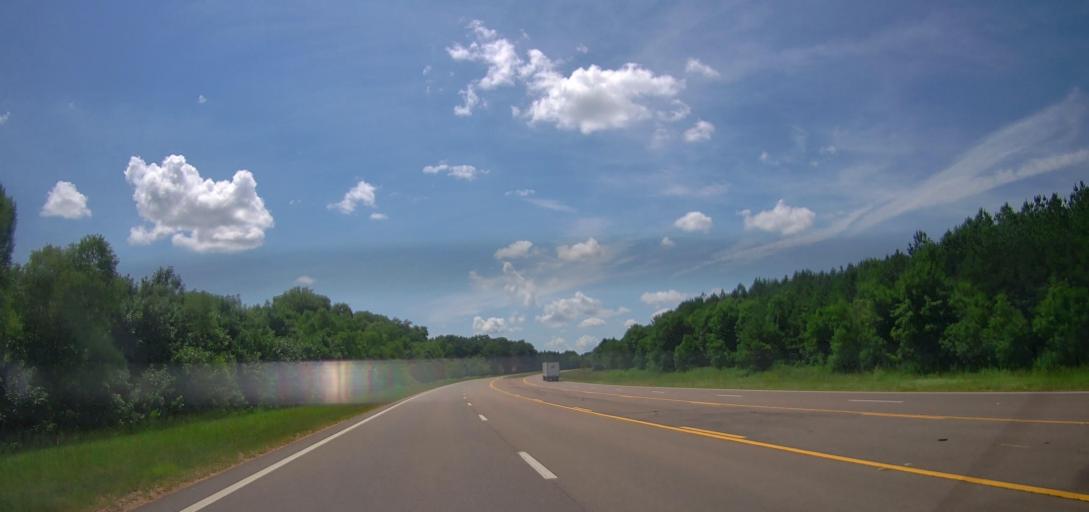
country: US
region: Mississippi
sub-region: Monroe County
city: Aberdeen
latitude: 33.8147
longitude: -88.5702
